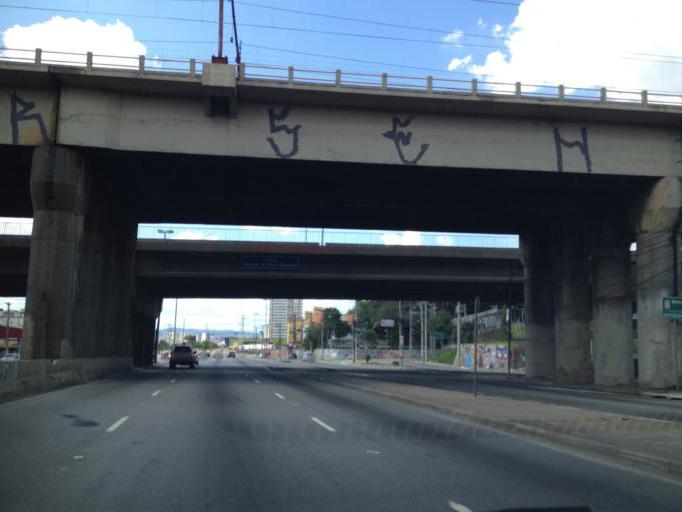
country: BR
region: Sao Paulo
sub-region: Sao Paulo
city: Sao Paulo
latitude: -23.5412
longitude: -46.5807
